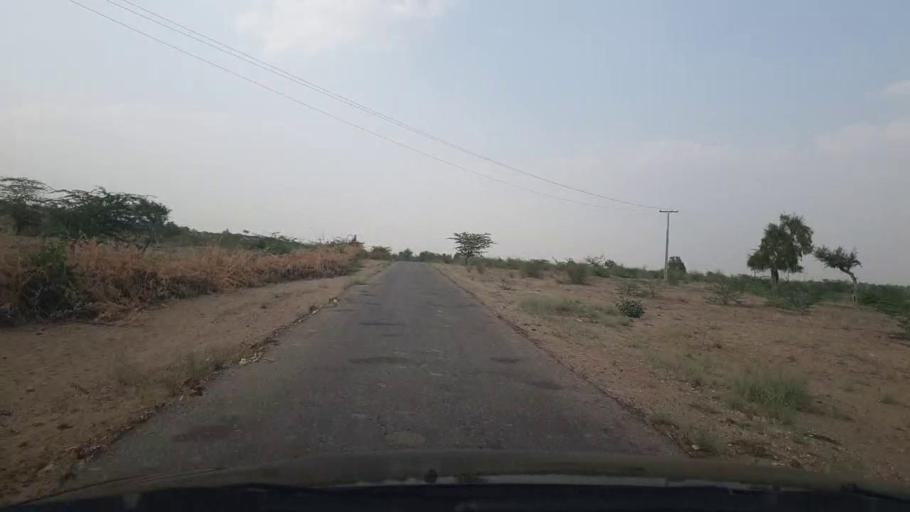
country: PK
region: Sindh
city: Islamkot
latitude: 25.0333
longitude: 70.5548
